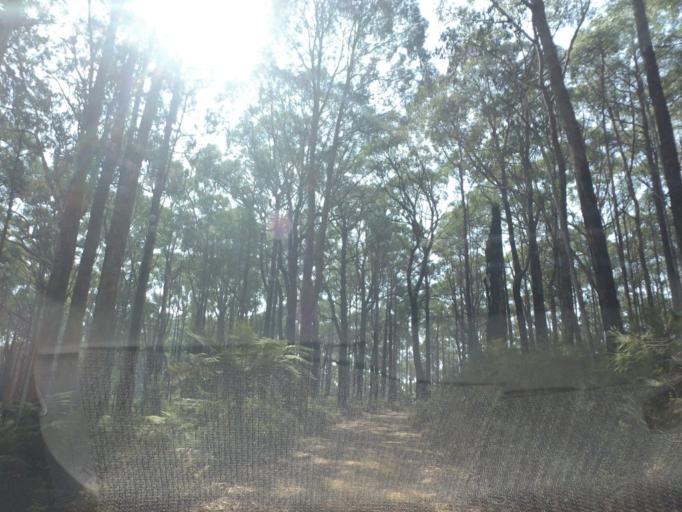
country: AU
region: Victoria
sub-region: Yarra Ranges
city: Millgrove
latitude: -37.5772
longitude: 145.6879
